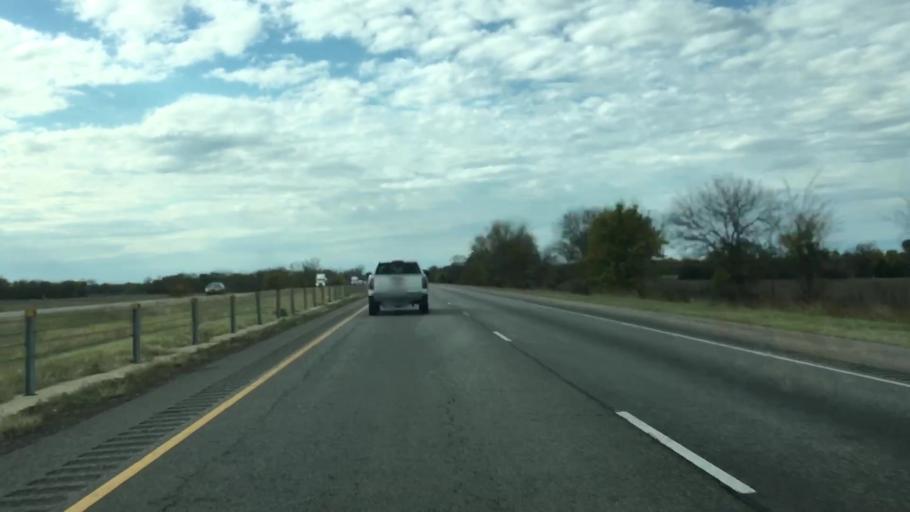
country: US
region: Arkansas
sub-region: Conway County
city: Morrilton
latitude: 35.1918
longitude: -92.7891
